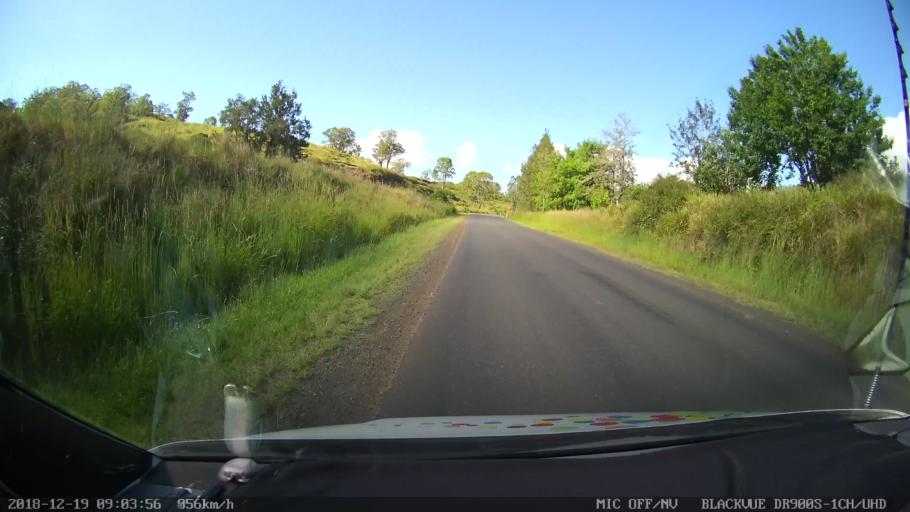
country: AU
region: New South Wales
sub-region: Kyogle
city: Kyogle
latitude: -28.4514
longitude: 152.9484
